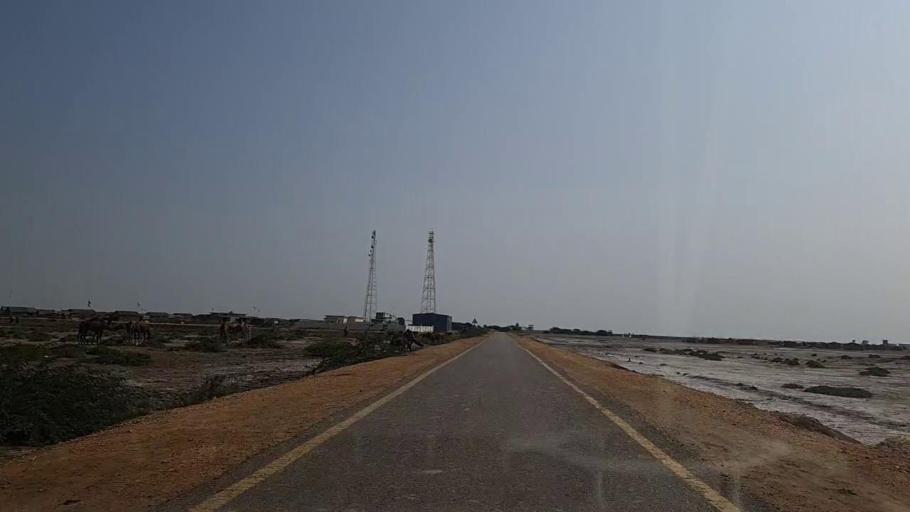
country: PK
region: Sindh
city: Chuhar Jamali
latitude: 24.1668
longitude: 67.8979
